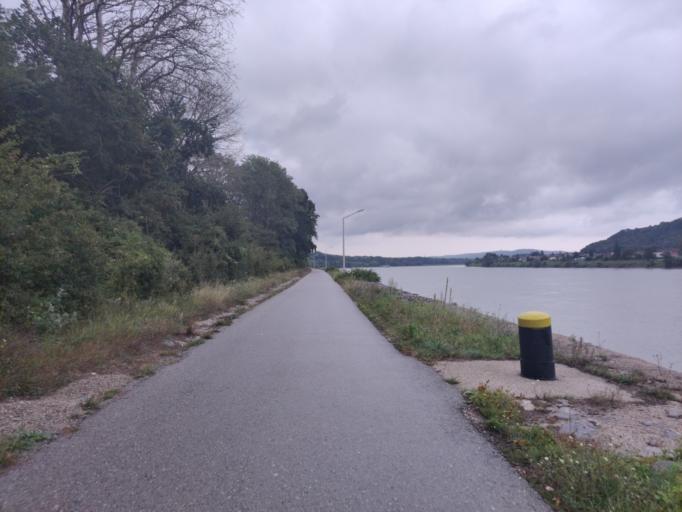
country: AT
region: Lower Austria
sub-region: Politischer Bezirk Korneuburg
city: Spillern
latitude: 48.3545
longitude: 16.2690
